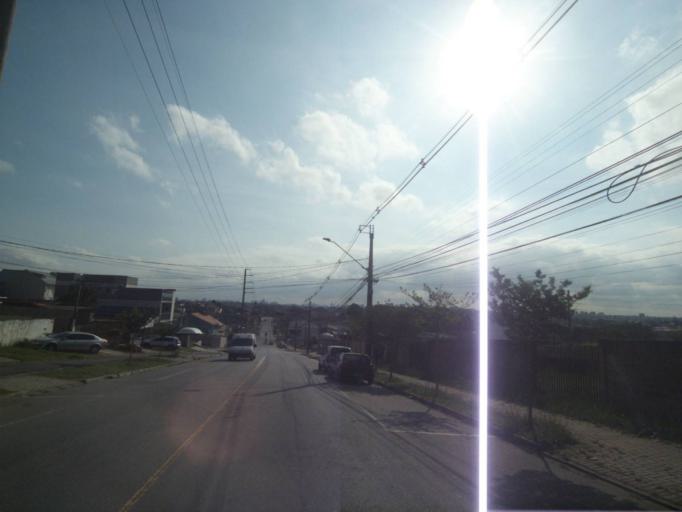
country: BR
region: Parana
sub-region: Pinhais
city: Pinhais
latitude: -25.4079
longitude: -49.2107
